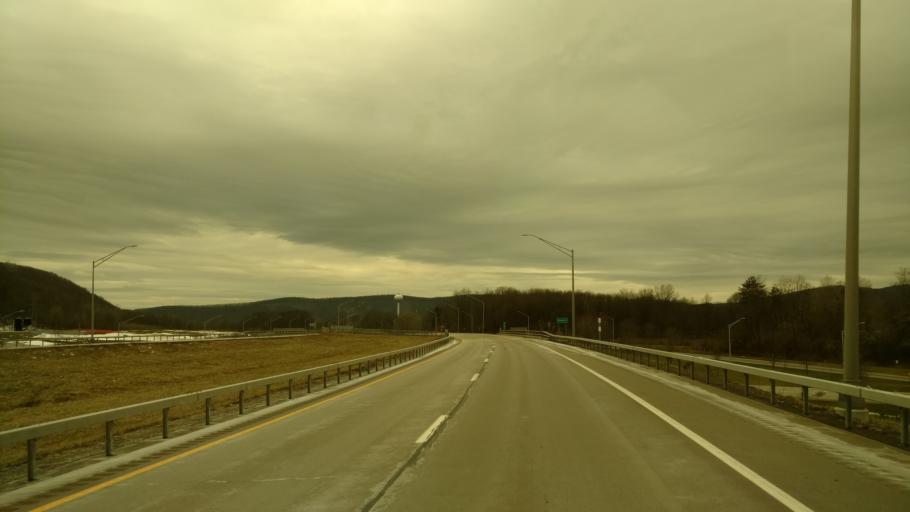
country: US
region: New York
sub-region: Cattaraugus County
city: Salamanca
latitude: 42.1543
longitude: -78.7498
